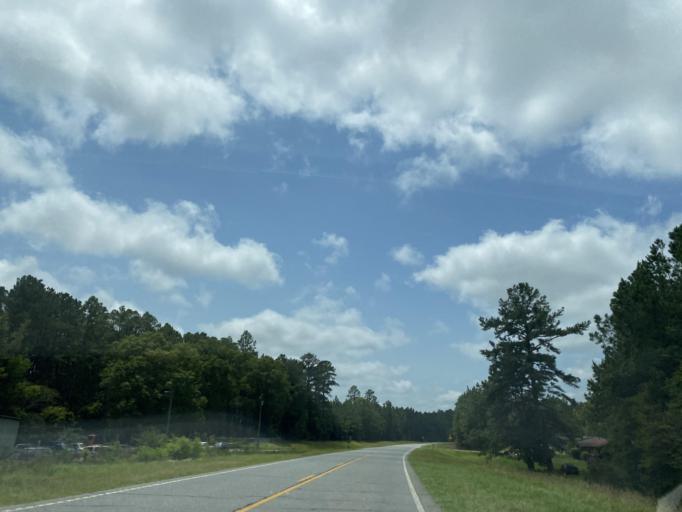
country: US
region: Georgia
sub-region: Wheeler County
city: Alamo
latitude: 32.1275
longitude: -82.7870
